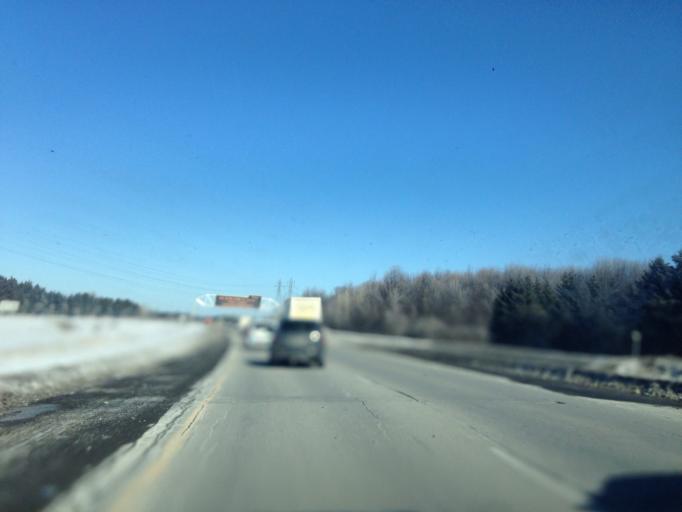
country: CA
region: Ontario
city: Ottawa
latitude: 45.4016
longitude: -75.5940
